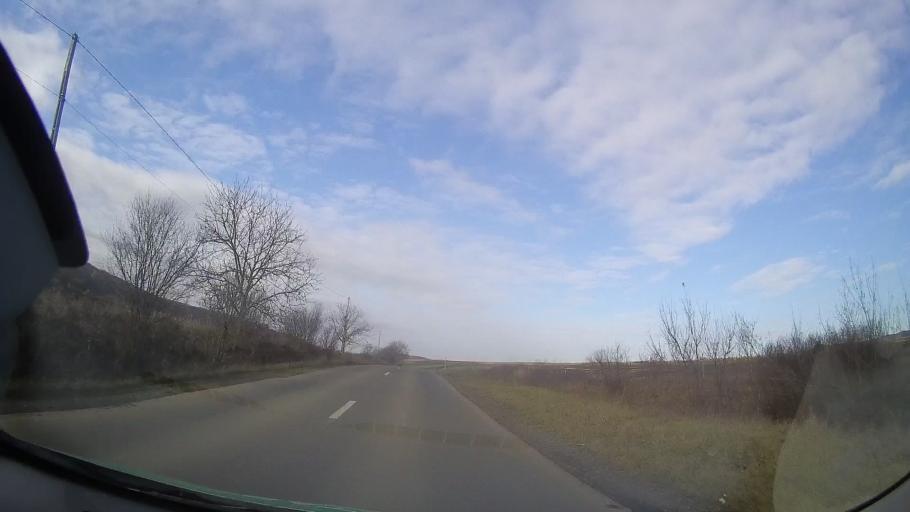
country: RO
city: Barza
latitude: 46.5512
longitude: 24.1141
